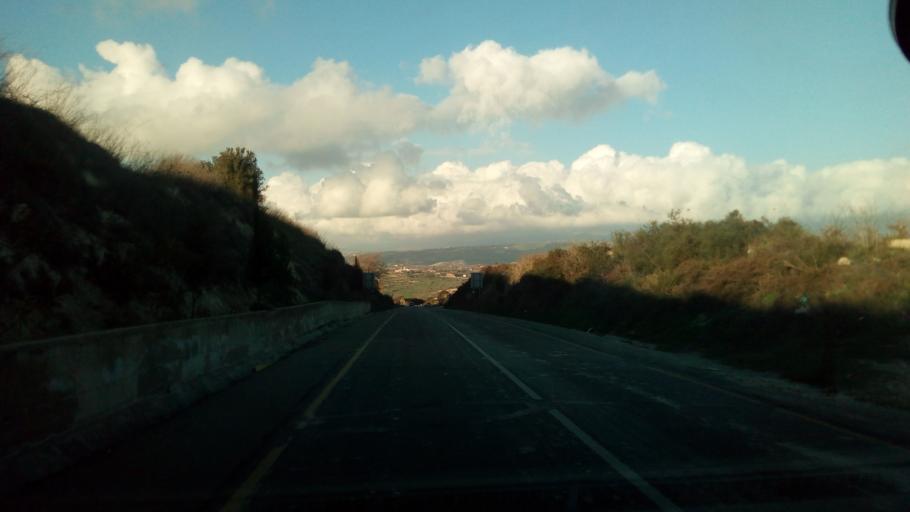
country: CY
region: Pafos
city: Mesogi
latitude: 34.8545
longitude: 32.4955
